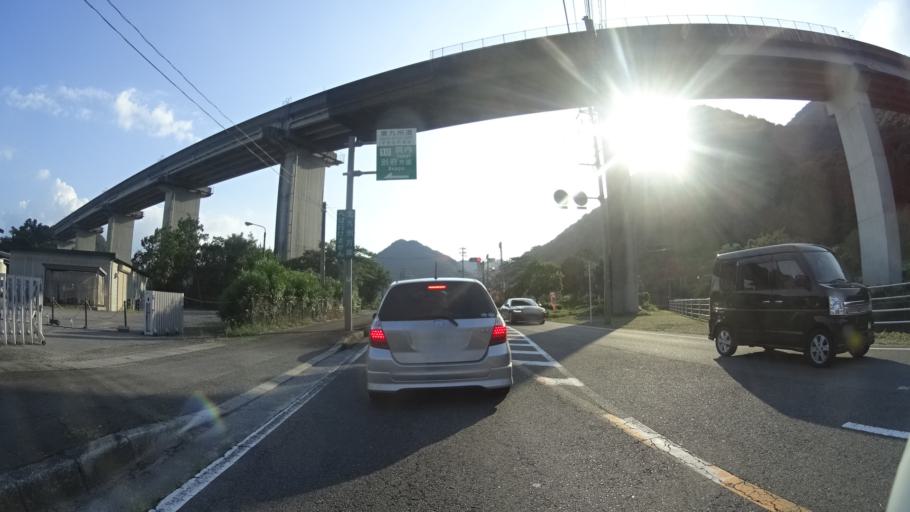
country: JP
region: Oita
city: Bungo-Takada-shi
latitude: 33.4785
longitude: 131.3333
